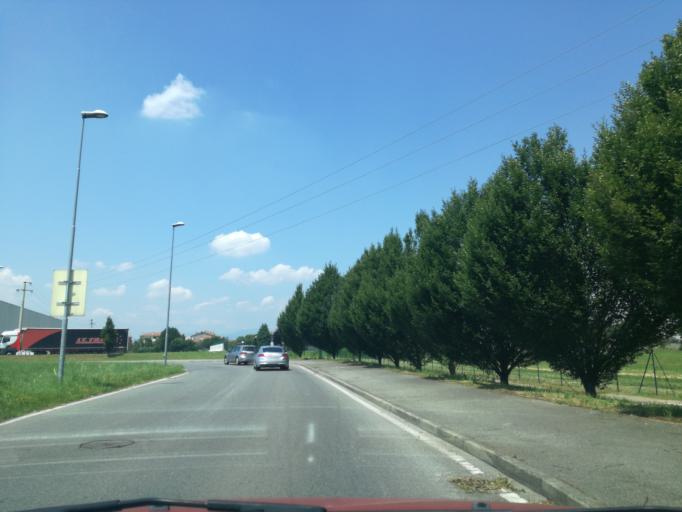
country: IT
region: Lombardy
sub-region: Provincia di Monza e Brianza
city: Biassono
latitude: 45.6273
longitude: 9.2550
